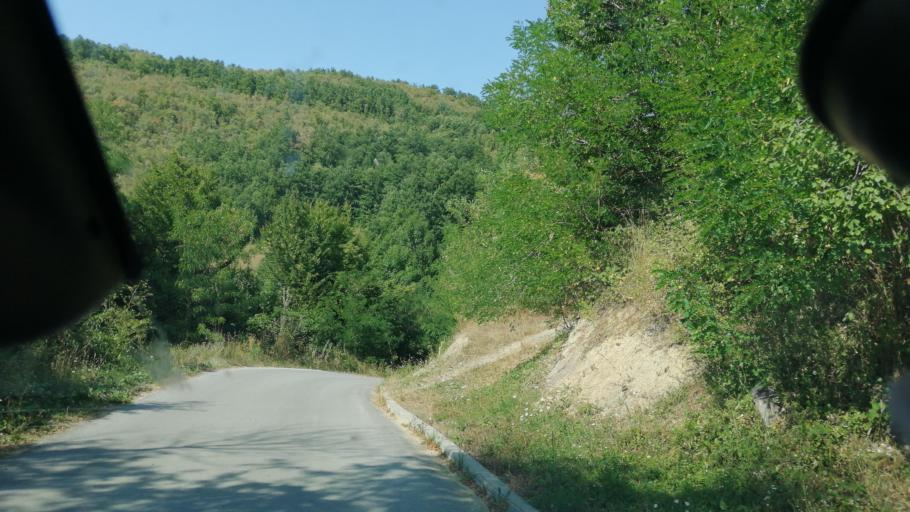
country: RS
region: Central Serbia
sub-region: Moravicki Okrug
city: Ivanjica
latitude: 43.6222
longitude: 20.2503
